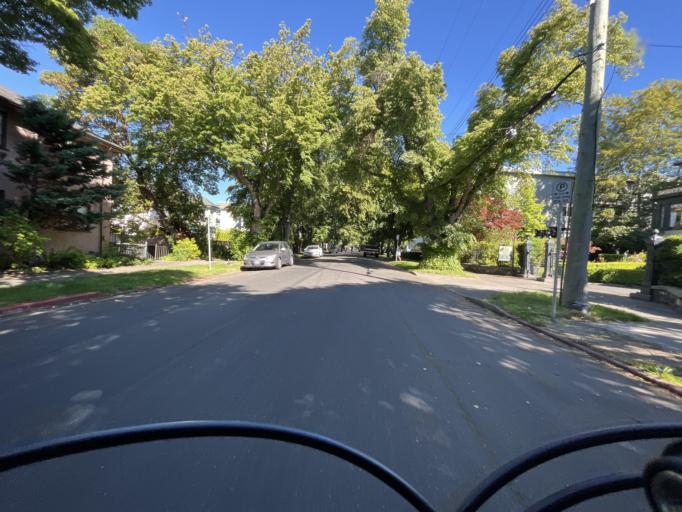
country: CA
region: British Columbia
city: Victoria
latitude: 48.4175
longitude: -123.3589
